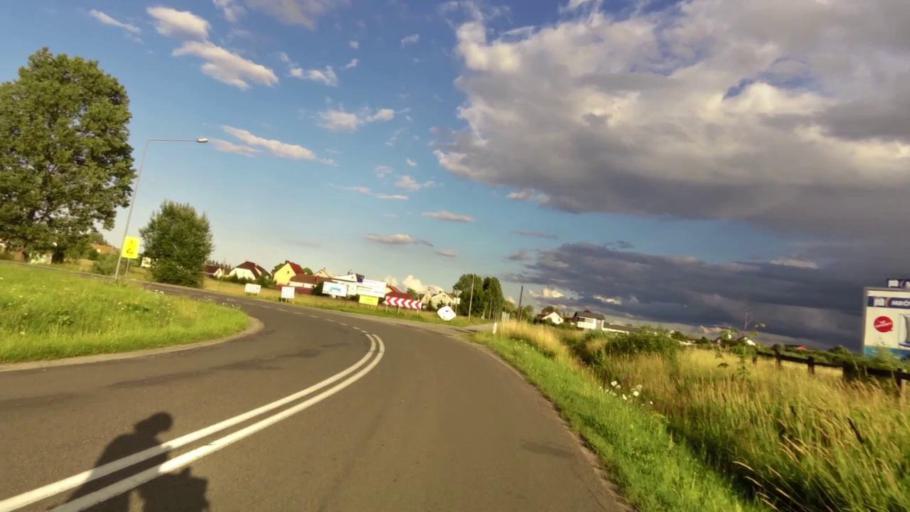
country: PL
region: West Pomeranian Voivodeship
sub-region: Powiat slawienski
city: Darlowo
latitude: 54.4134
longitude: 16.4051
